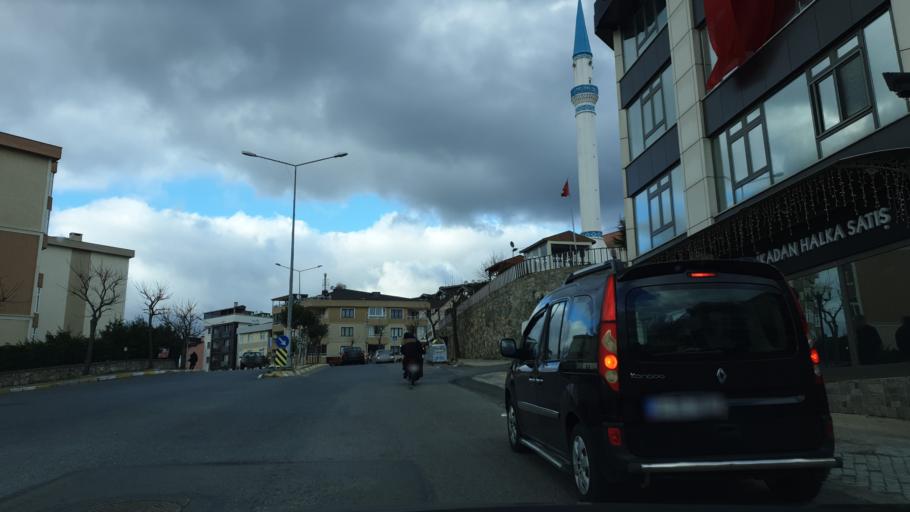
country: TR
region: Istanbul
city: Pendik
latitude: 40.9038
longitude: 29.2470
